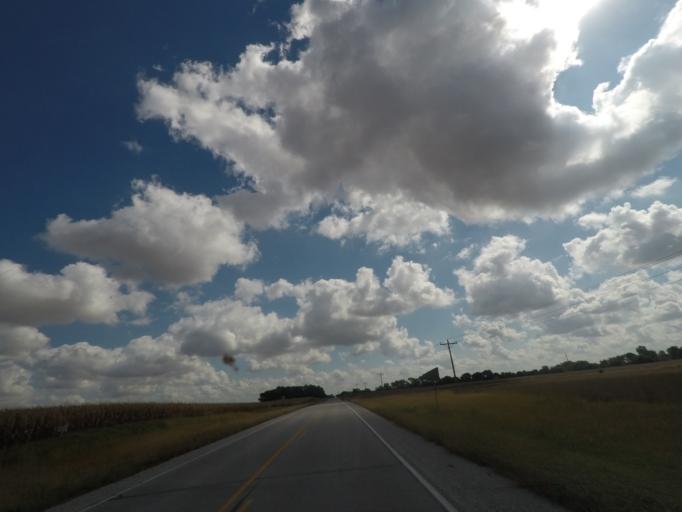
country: US
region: Iowa
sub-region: Story County
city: Nevada
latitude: 42.0226
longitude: -93.3587
